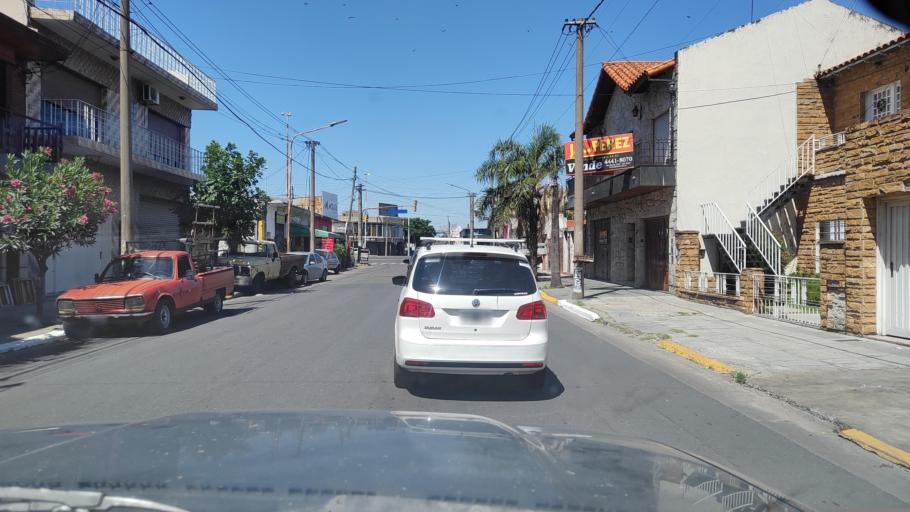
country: AR
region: Buenos Aires
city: San Justo
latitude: -34.6830
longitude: -58.5660
